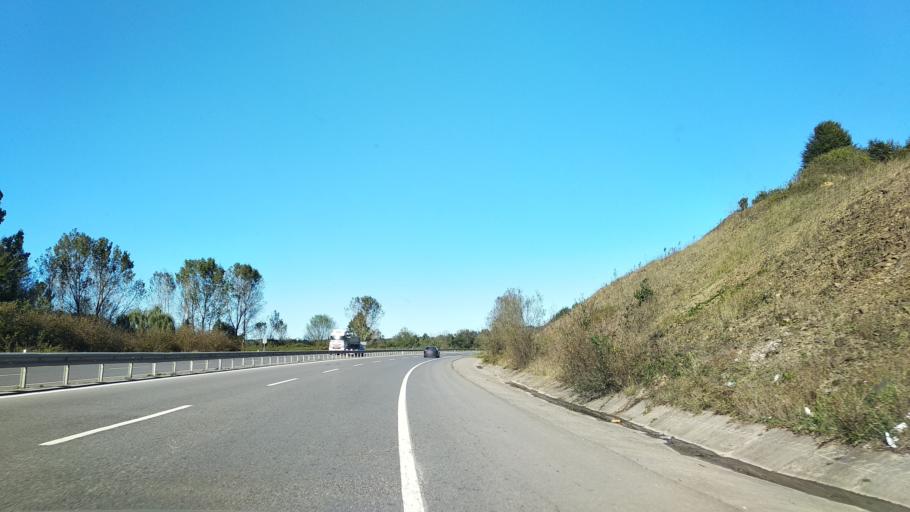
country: TR
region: Sakarya
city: Karasu
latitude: 41.0606
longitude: 30.6374
